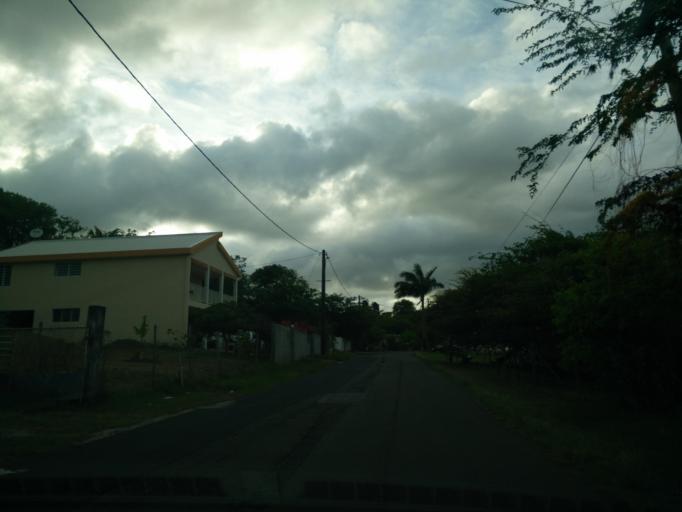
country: MQ
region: Martinique
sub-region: Martinique
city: Le Marin
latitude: 14.4570
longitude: -60.8411
